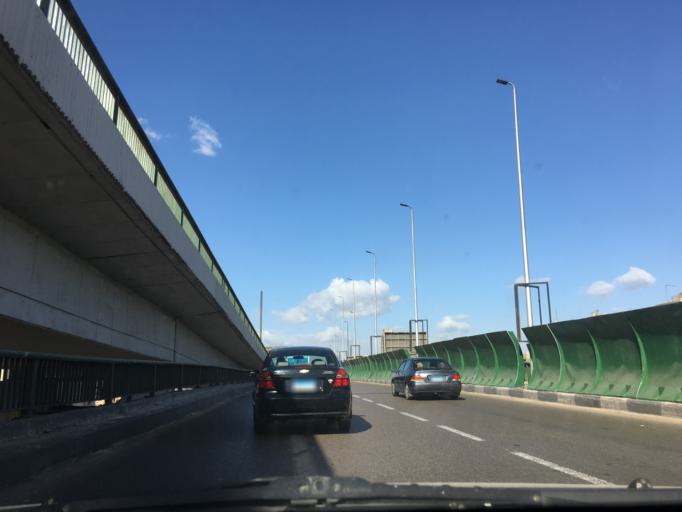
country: EG
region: Muhafazat al Qahirah
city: Cairo
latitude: 30.0595
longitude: 31.3023
